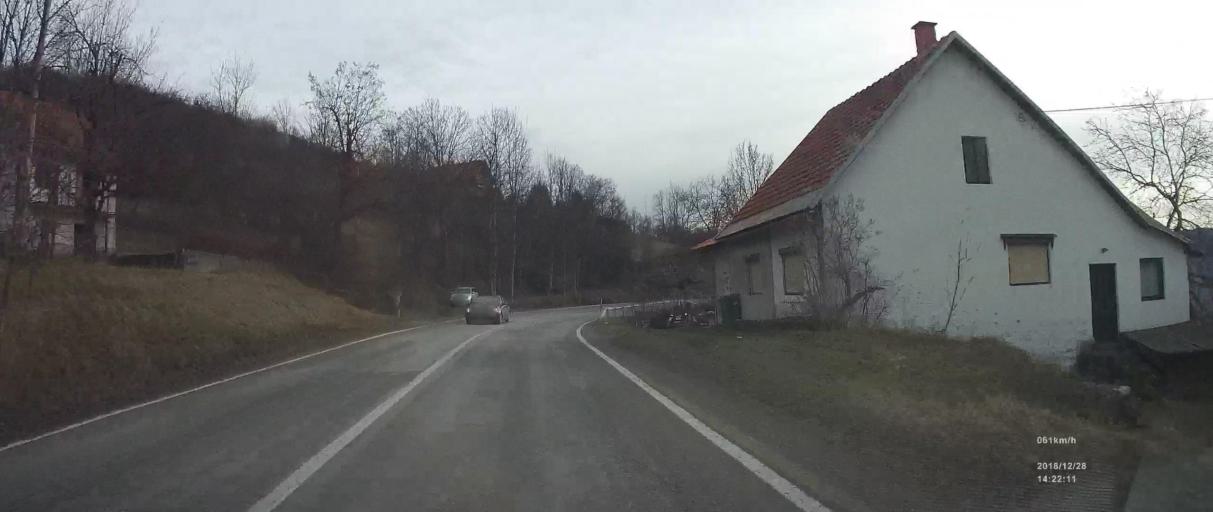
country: HR
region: Primorsko-Goranska
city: Vrbovsko
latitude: 45.3874
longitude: 15.0858
